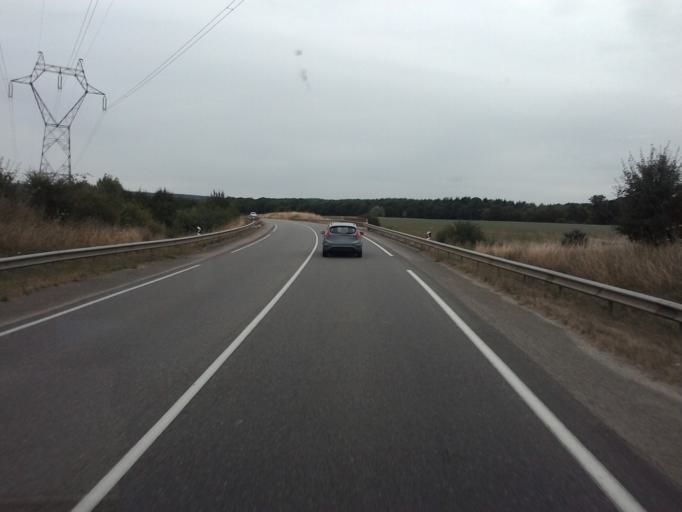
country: FR
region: Lorraine
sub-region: Departement de Meurthe-et-Moselle
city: Bainville-sur-Madon
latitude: 48.5851
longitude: 6.1089
